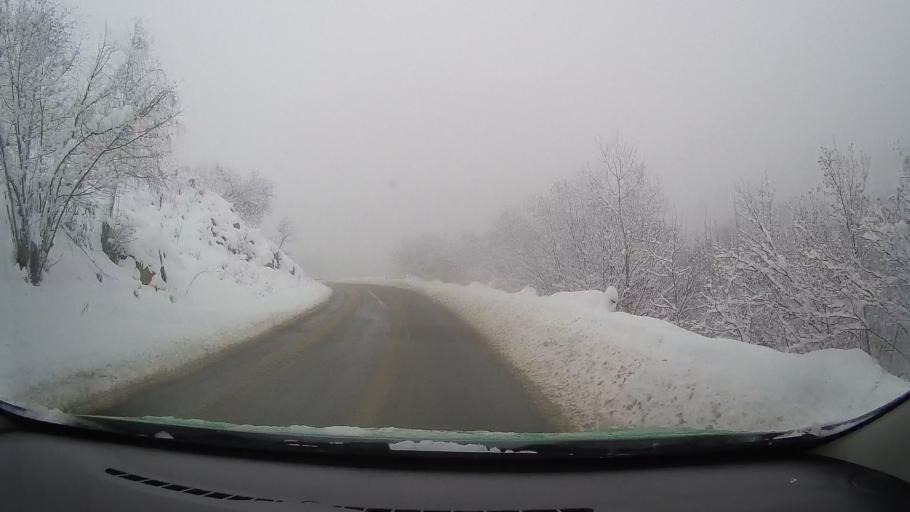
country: RO
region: Sibiu
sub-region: Comuna Poiana Sibiului
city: Poiana Sibiului
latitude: 45.7969
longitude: 23.7864
